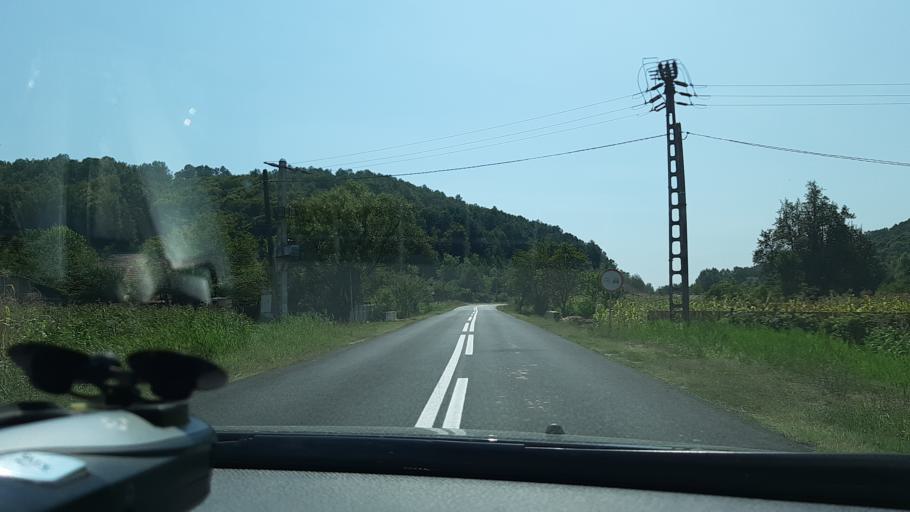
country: RO
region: Gorj
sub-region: Comuna Licuriciu
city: Licuriciu
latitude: 44.9128
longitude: 23.6222
